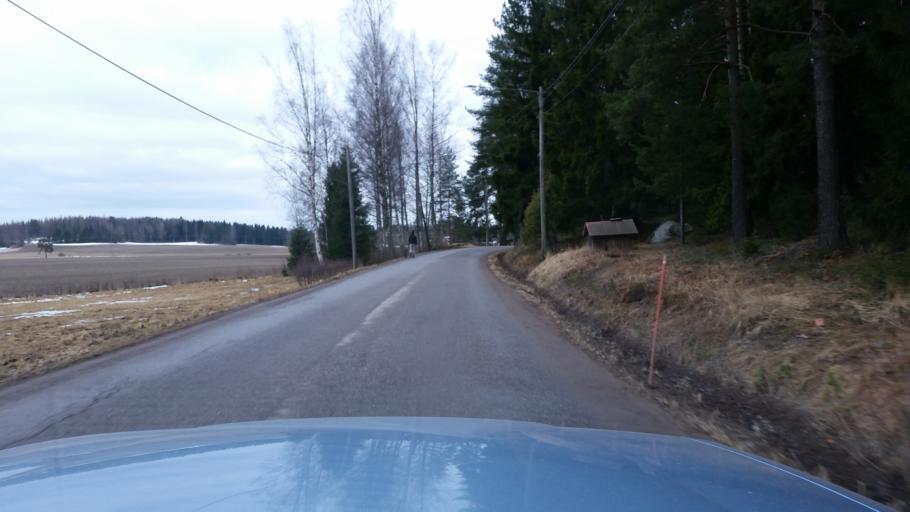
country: FI
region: Uusimaa
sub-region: Helsinki
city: Espoo
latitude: 60.2833
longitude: 24.6757
